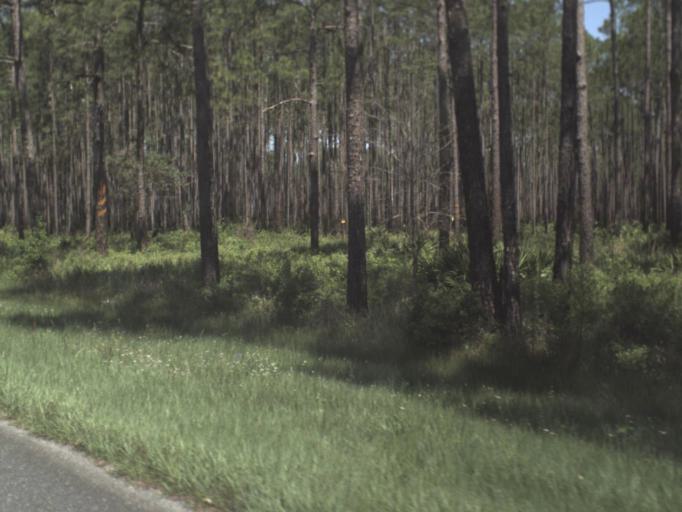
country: US
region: Florida
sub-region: Columbia County
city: Watertown
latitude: 30.1884
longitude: -82.5424
